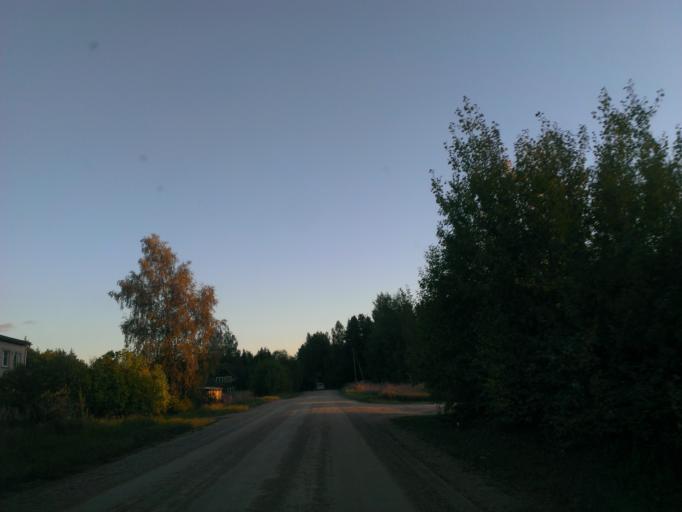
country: LV
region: Incukalns
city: Vangazi
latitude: 57.1033
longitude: 24.5631
